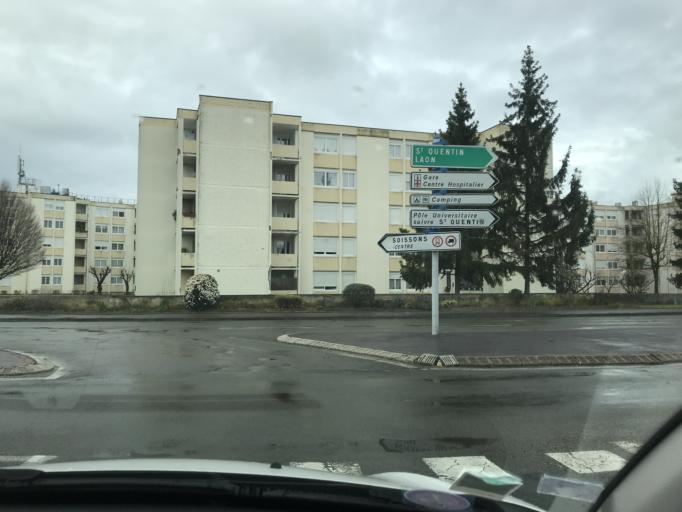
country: FR
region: Picardie
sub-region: Departement de l'Aisne
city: Belleu
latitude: 49.3675
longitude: 3.3333
